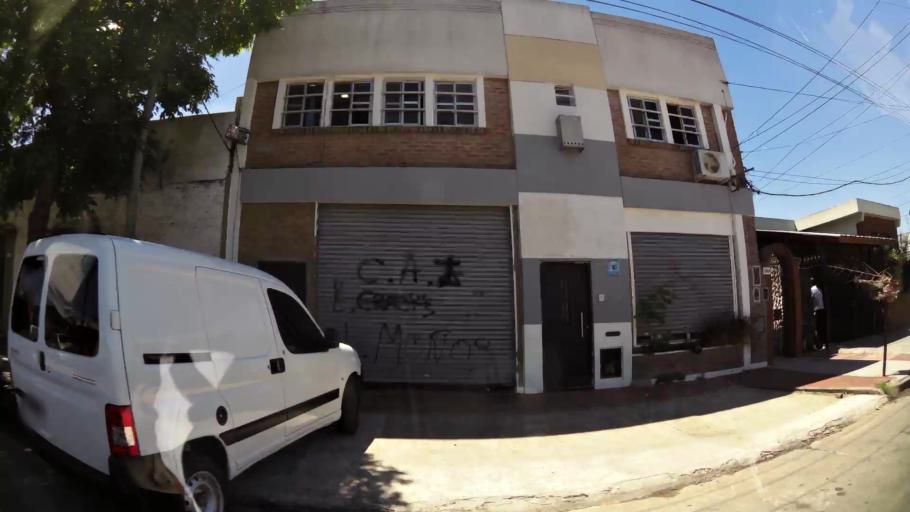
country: AR
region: Buenos Aires
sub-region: Partido de Quilmes
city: Quilmes
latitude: -34.7186
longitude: -58.3119
